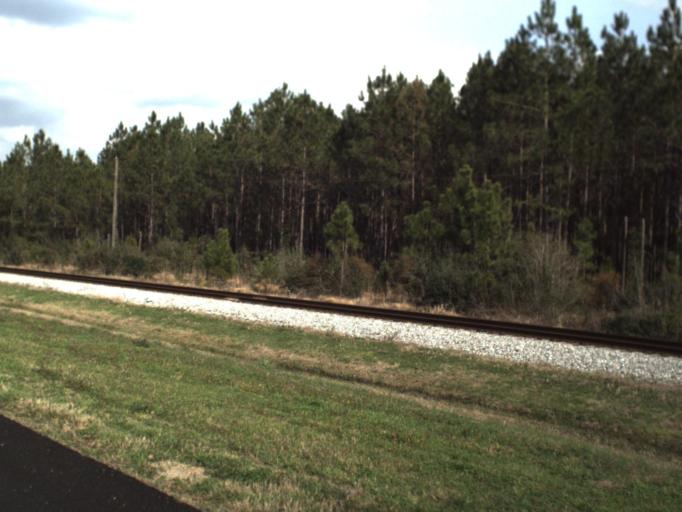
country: US
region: Florida
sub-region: Bay County
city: Youngstown
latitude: 30.3284
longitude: -85.4470
